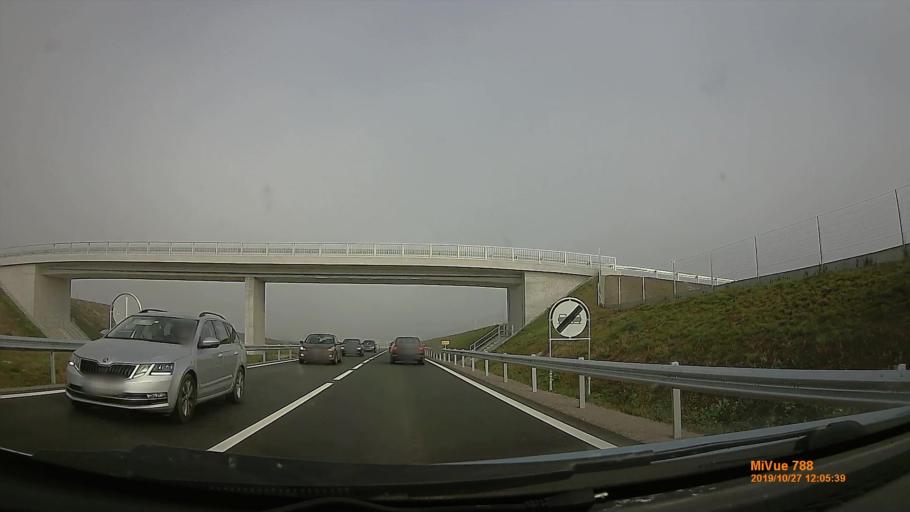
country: AT
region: Lower Austria
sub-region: Politischer Bezirk Mistelbach
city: Drasenhofen
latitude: 48.7658
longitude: 16.6381
